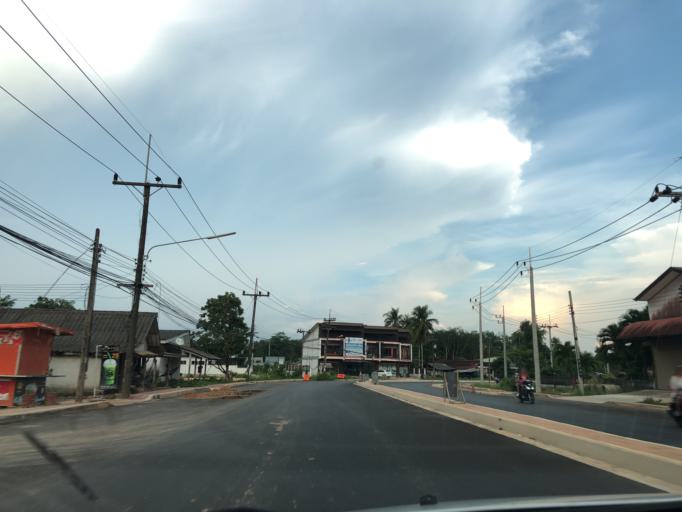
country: TH
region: Phangnga
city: Ban Ao Nang
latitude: 8.0701
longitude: 98.8402
